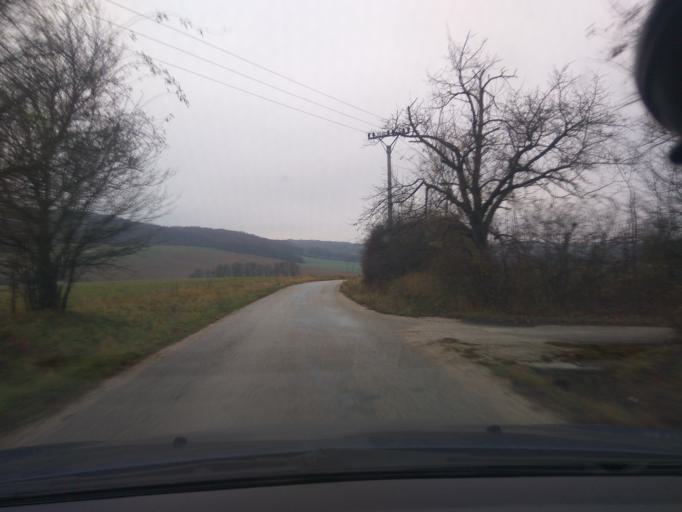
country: SK
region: Trnavsky
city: Vrbove
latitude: 48.6846
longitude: 17.6738
